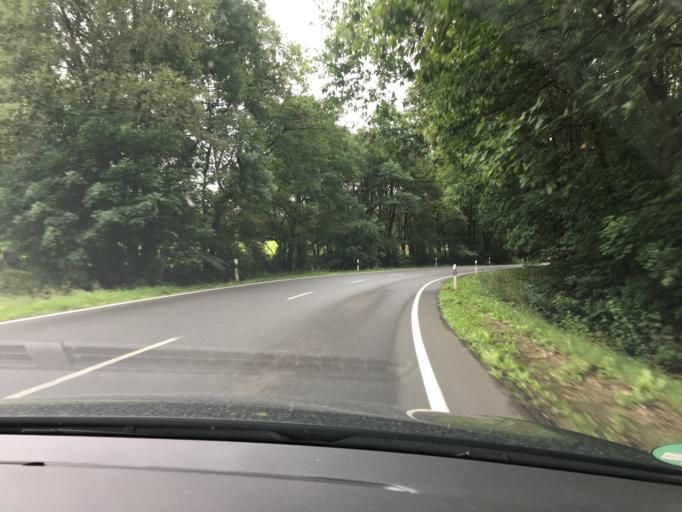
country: DE
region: North Rhine-Westphalia
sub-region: Regierungsbezirk Koln
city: Hurtgenwald
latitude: 50.7405
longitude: 6.3960
